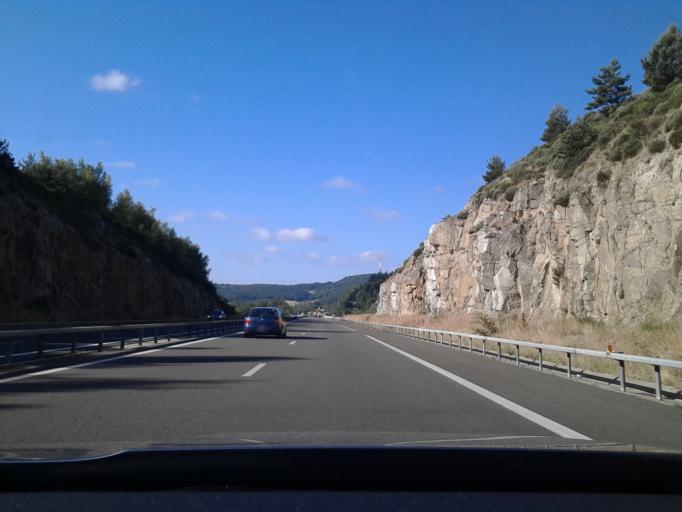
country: FR
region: Languedoc-Roussillon
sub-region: Departement de la Lozere
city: Aumont-Aubrac
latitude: 44.6443
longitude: 3.2430
